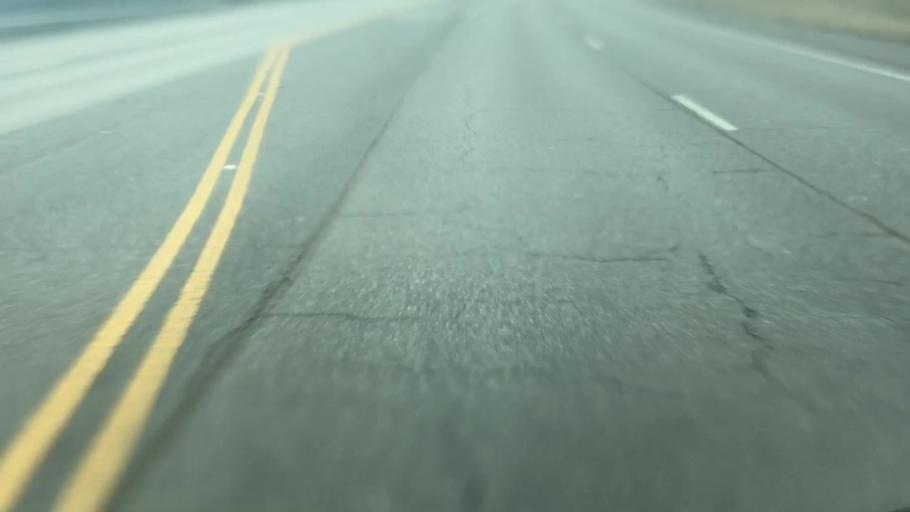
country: US
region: Alabama
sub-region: Walker County
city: Jasper
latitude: 33.8164
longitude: -87.2332
